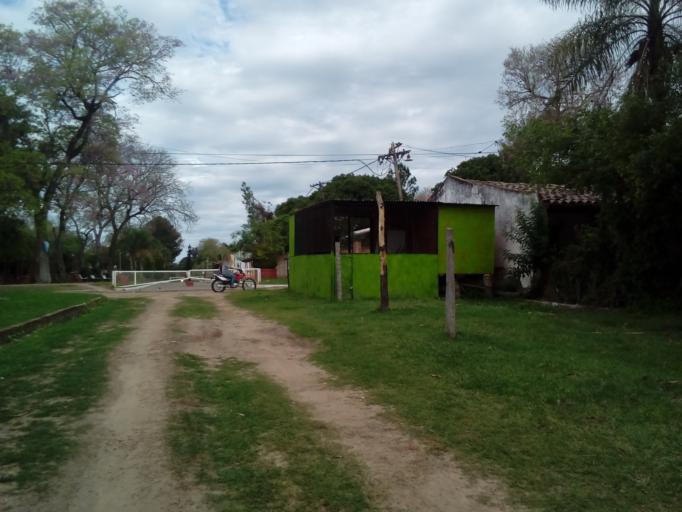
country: AR
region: Corrientes
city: San Luis del Palmar
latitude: -27.4558
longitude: -58.6558
